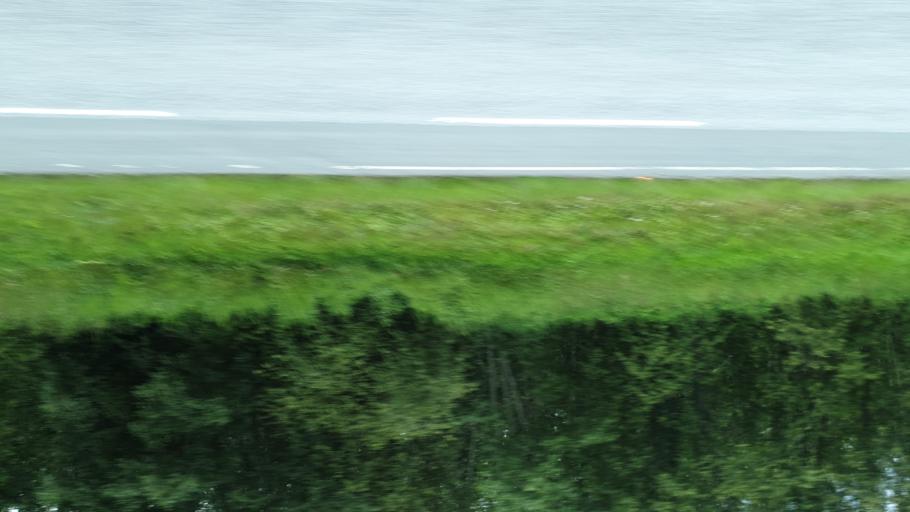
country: NO
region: Sor-Trondelag
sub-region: Midtre Gauldal
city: Storen
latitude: 63.0896
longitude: 10.2501
